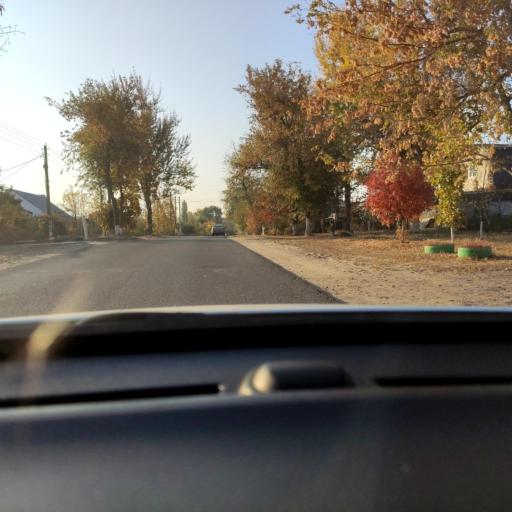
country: RU
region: Voronezj
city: Somovo
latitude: 51.6911
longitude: 39.3182
